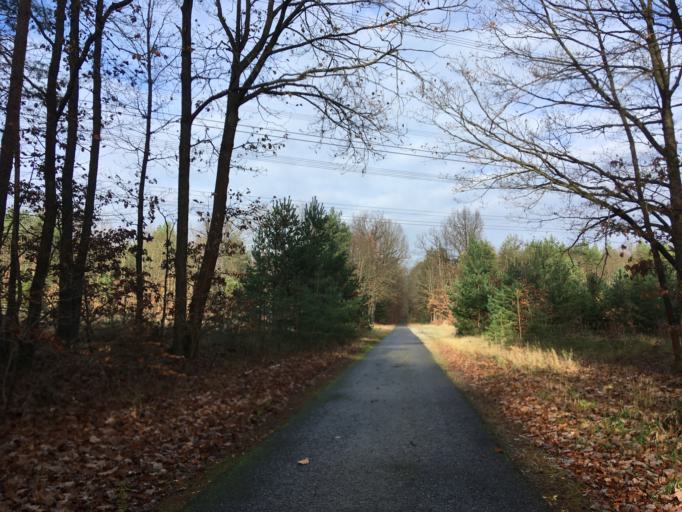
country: DE
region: Brandenburg
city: Tauer
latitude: 51.9290
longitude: 14.5113
